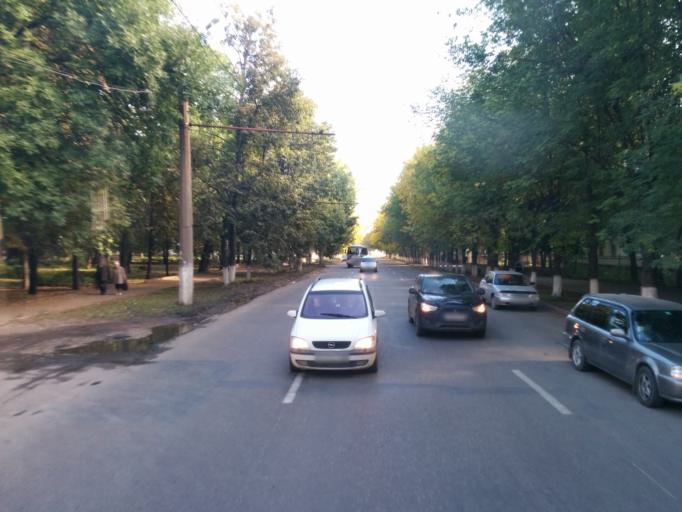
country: RU
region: Bashkortostan
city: Ufa
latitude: 54.8218
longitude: 56.0676
